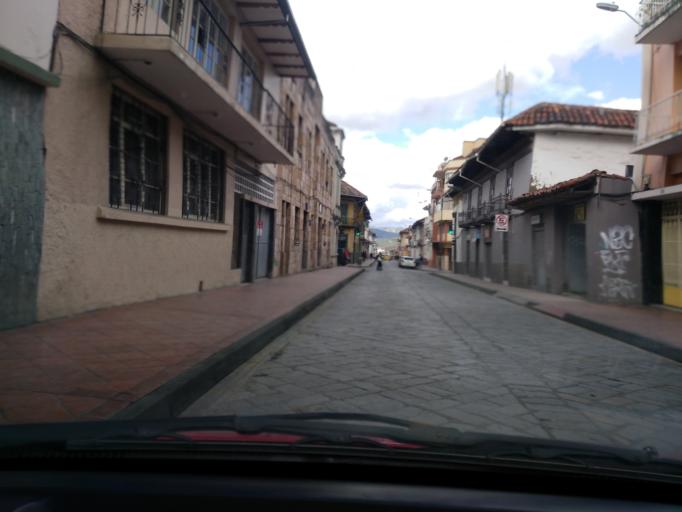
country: EC
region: Azuay
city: Cuenca
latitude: -2.8999
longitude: -79.0050
